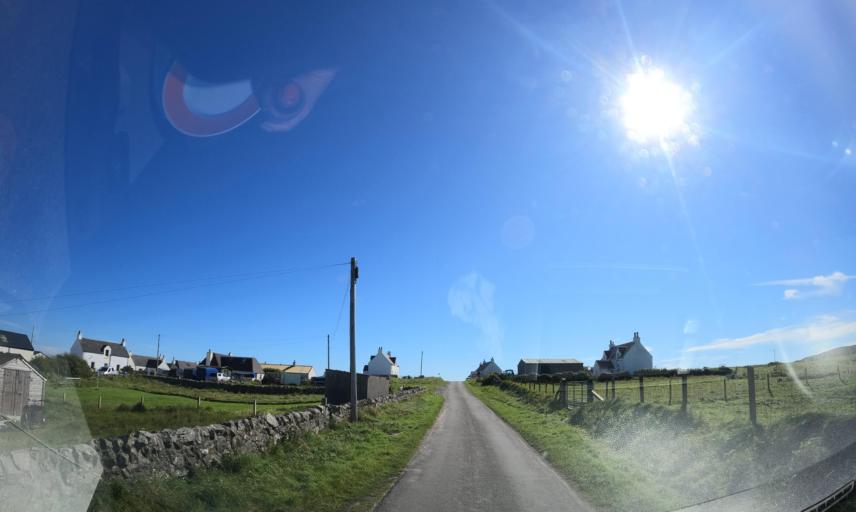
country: GB
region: Scotland
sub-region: Eilean Siar
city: Barra
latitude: 56.4666
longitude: -6.8965
